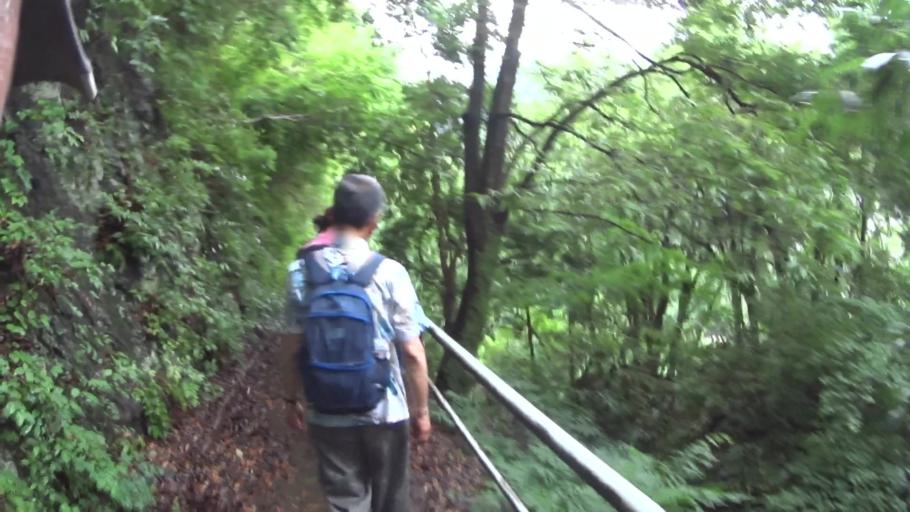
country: JP
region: Tokyo
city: Itsukaichi
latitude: 35.8050
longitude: 139.0917
